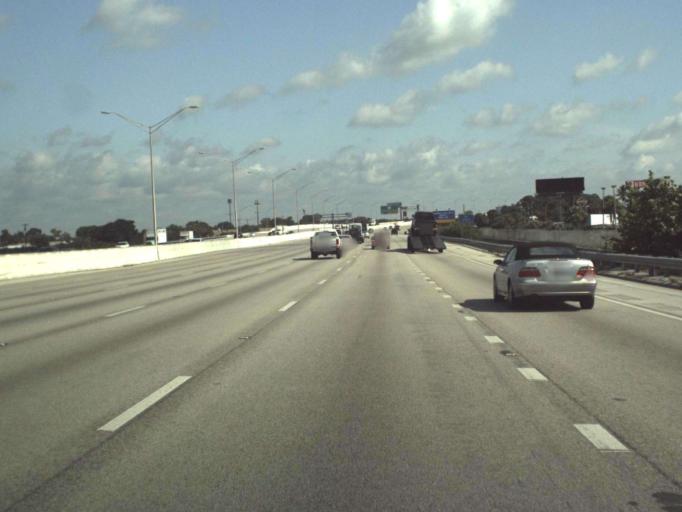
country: US
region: Florida
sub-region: Palm Beach County
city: Mangonia Park
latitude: 26.7752
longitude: -80.0973
